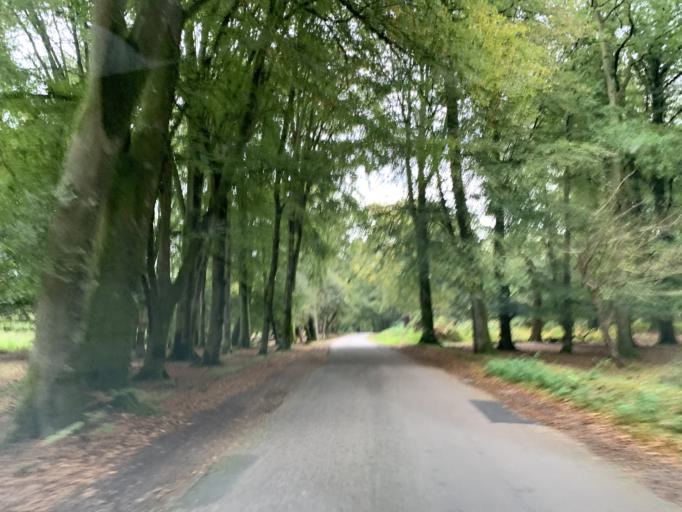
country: GB
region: England
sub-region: Hampshire
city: Lyndhurst
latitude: 50.8588
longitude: -1.6389
